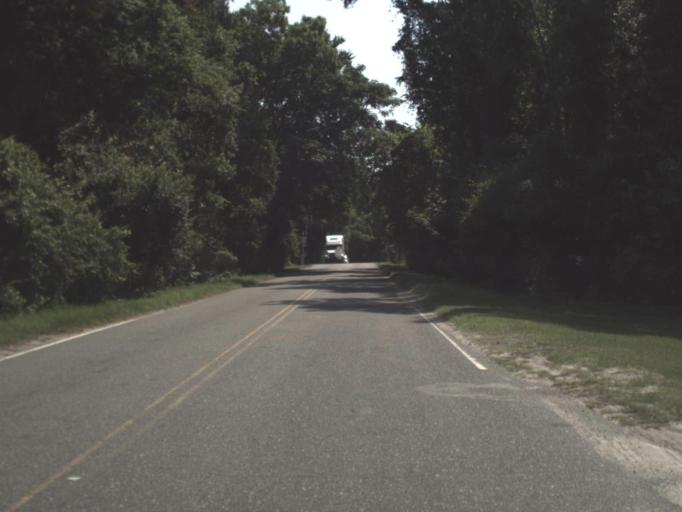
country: US
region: Florida
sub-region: Duval County
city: Jacksonville
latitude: 30.3712
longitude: -81.7325
